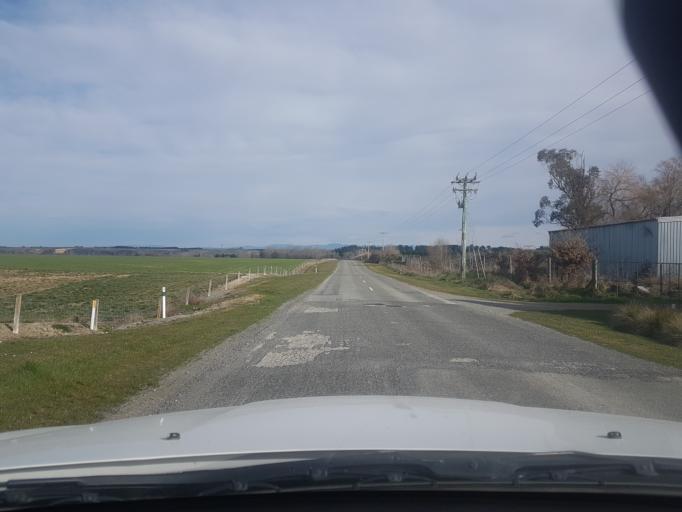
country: NZ
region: Canterbury
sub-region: Timaru District
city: Pleasant Point
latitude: -44.1223
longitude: 171.1955
